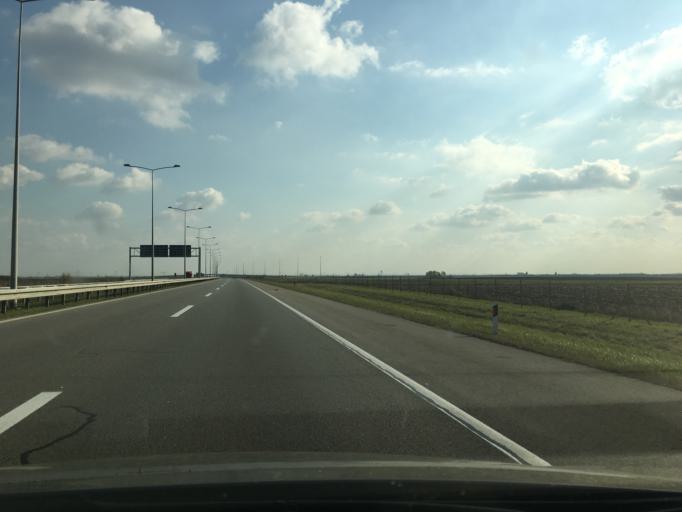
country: RS
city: Krcedin
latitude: 45.0988
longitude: 20.1152
